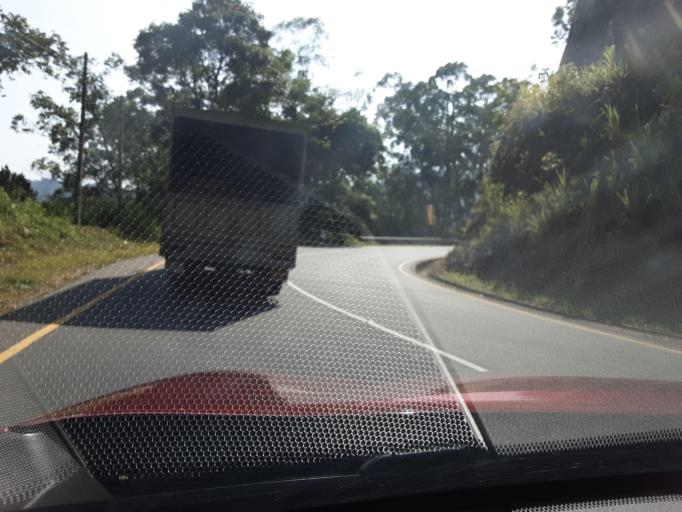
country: LK
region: Uva
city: Badulla
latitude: 6.9644
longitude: 81.0927
